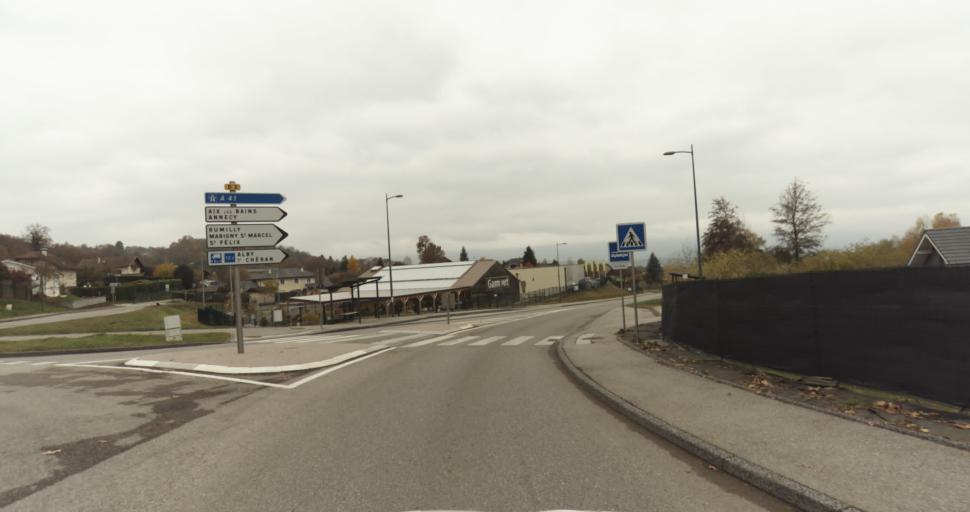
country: FR
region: Rhone-Alpes
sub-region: Departement de la Haute-Savoie
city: Alby-sur-Cheran
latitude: 45.8121
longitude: 6.0078
